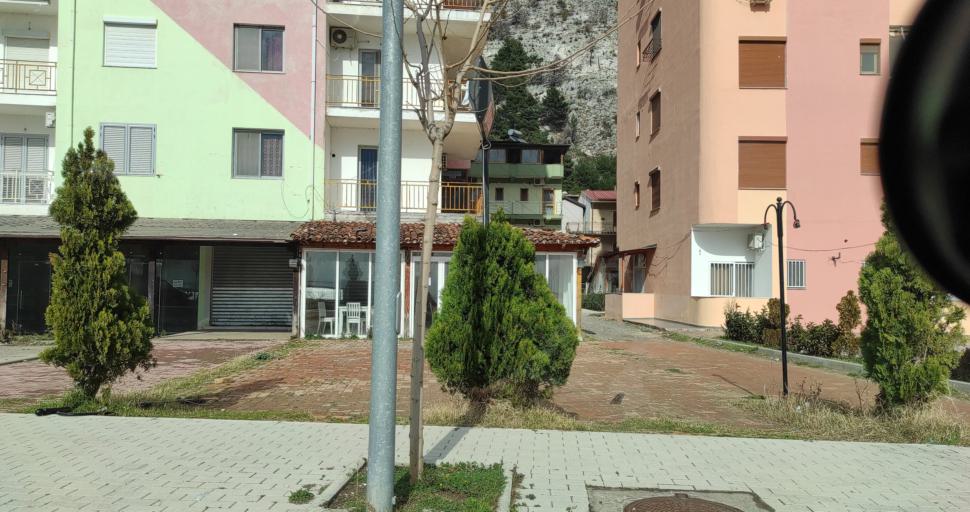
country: AL
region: Lezhe
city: Shengjin
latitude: 41.8136
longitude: 19.5913
